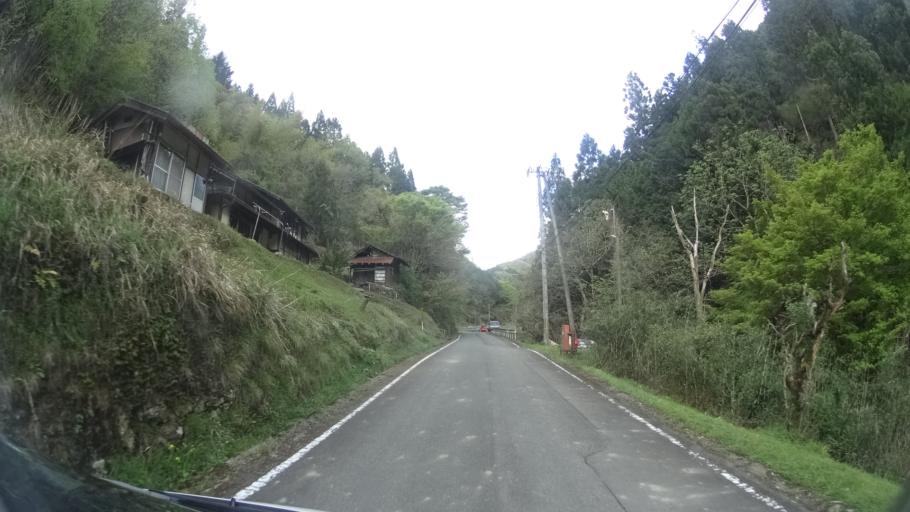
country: JP
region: Kyoto
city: Ayabe
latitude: 35.2468
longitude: 135.2961
